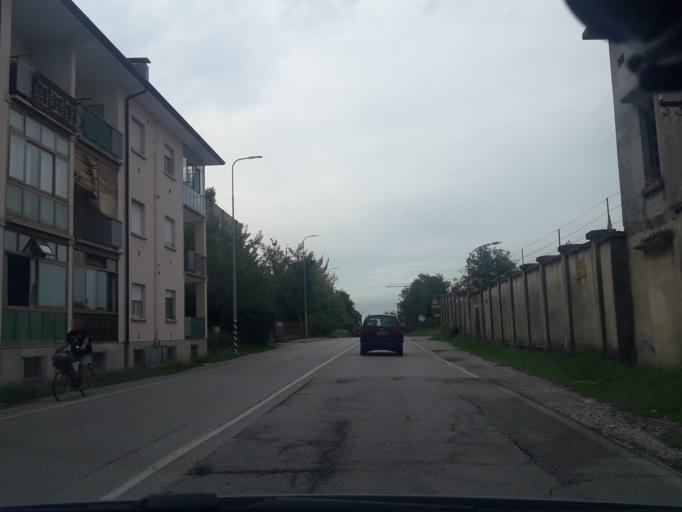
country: IT
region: Friuli Venezia Giulia
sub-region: Provincia di Udine
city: Udine
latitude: 46.0525
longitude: 13.2210
